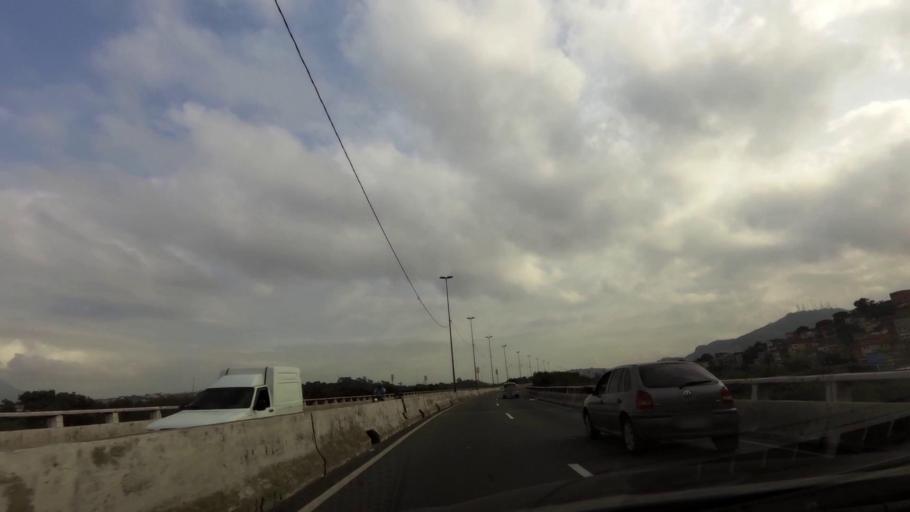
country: BR
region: Espirito Santo
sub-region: Vitoria
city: Vitoria
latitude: -20.3390
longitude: -40.3544
